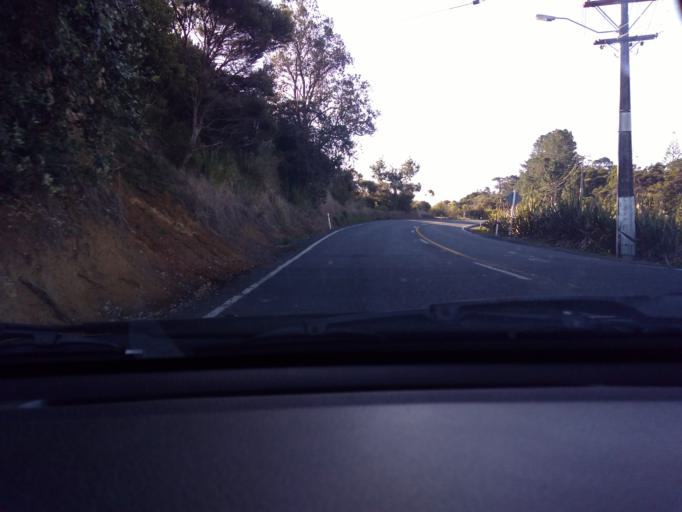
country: NZ
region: Auckland
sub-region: Auckland
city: Warkworth
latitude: -36.4070
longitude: 174.7189
